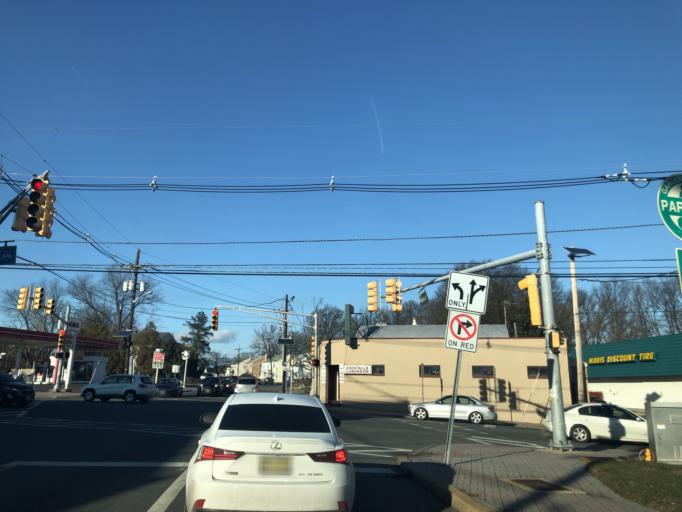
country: US
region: New Jersey
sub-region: Middlesex County
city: Fords
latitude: 40.5261
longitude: -74.3056
